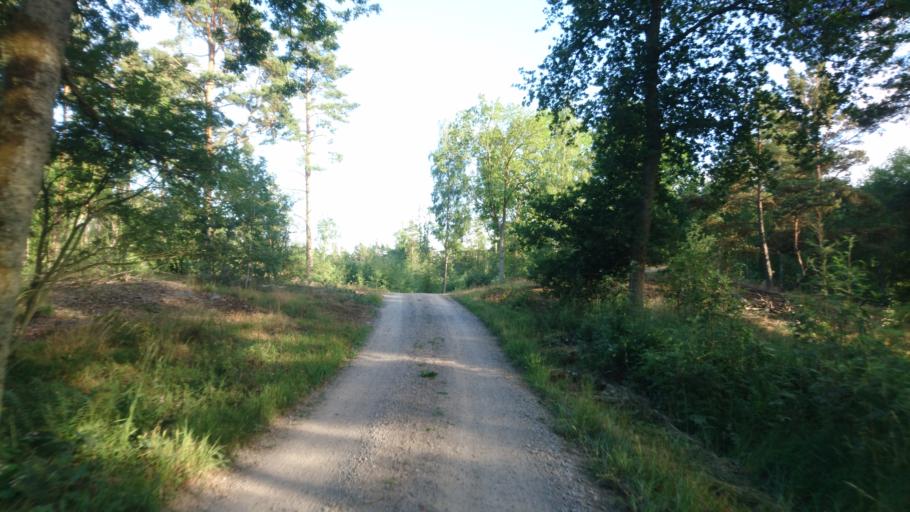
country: SE
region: Blekinge
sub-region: Karlshamns Kommun
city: Morrum
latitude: 56.1548
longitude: 14.7997
